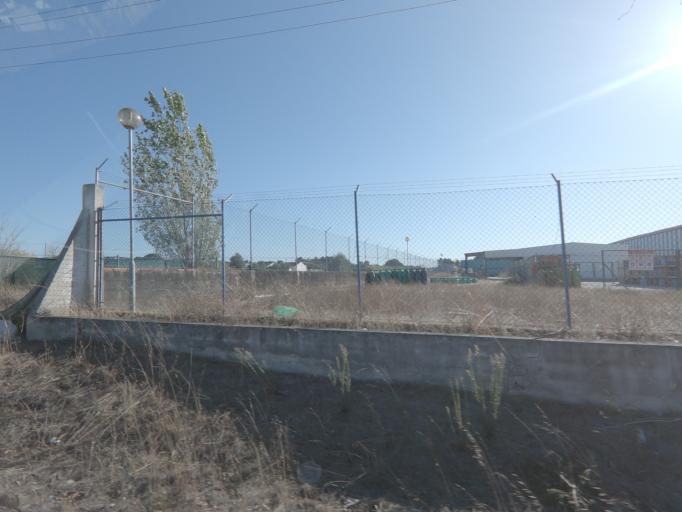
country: PT
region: Setubal
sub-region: Palmela
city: Pinhal Novo
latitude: 38.6089
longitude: -8.9443
